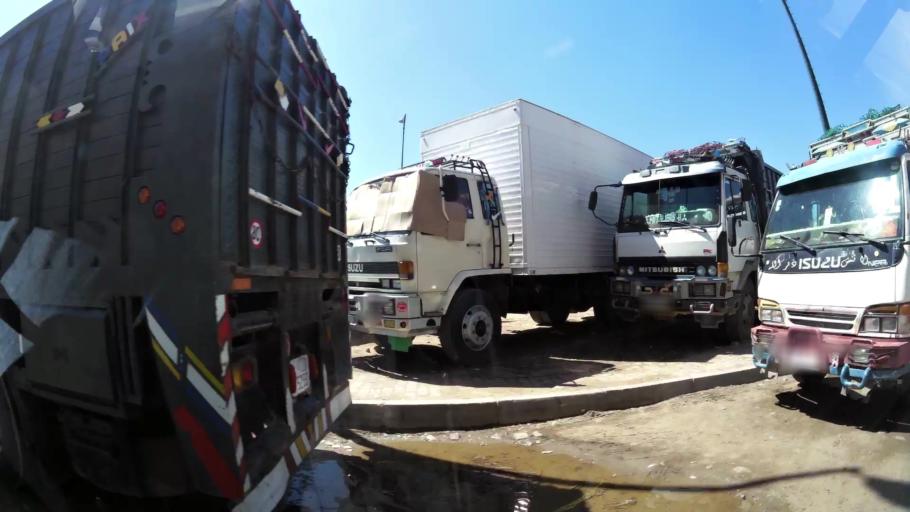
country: MA
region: Marrakech-Tensift-Al Haouz
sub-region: Marrakech
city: Marrakesh
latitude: 31.6282
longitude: -8.0637
